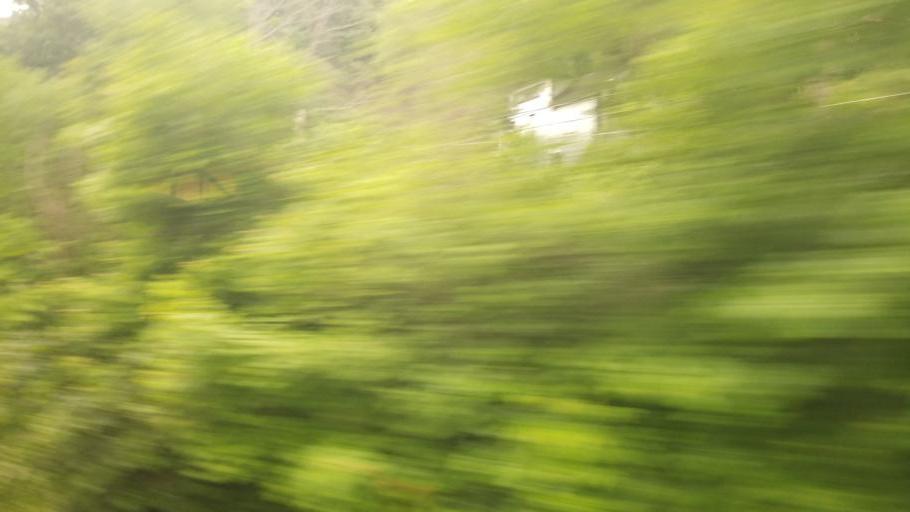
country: US
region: Pennsylvania
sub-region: Somerset County
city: Milford
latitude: 39.8121
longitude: -79.3289
